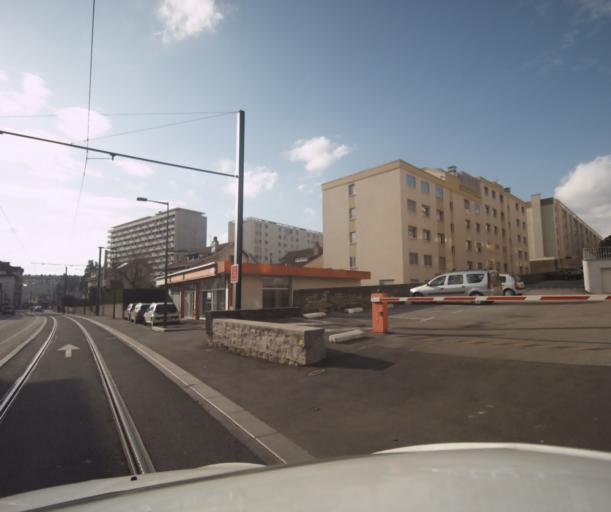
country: FR
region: Franche-Comte
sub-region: Departement du Doubs
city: Besancon
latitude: 47.2491
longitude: 6.0396
